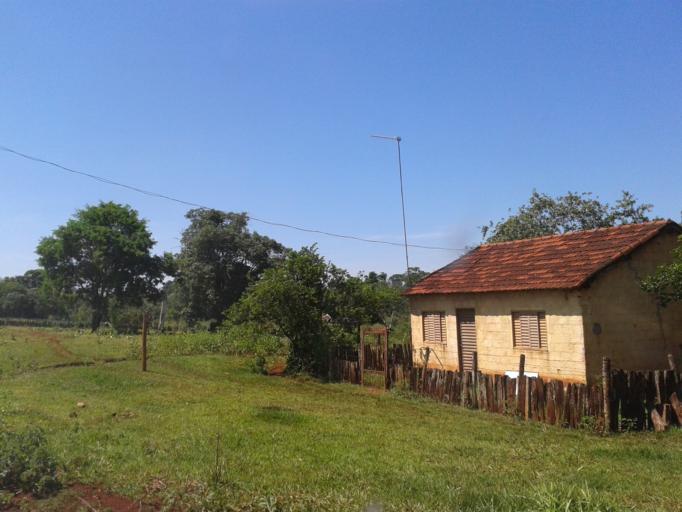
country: BR
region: Minas Gerais
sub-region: Centralina
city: Centralina
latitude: -18.6372
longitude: -49.2957
